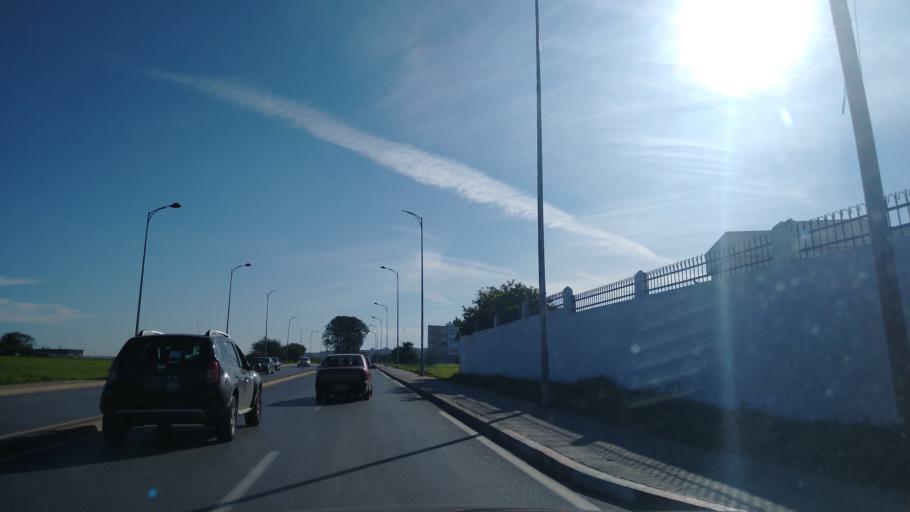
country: MA
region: Rabat-Sale-Zemmour-Zaer
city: Sale
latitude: 34.0190
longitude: -6.7348
